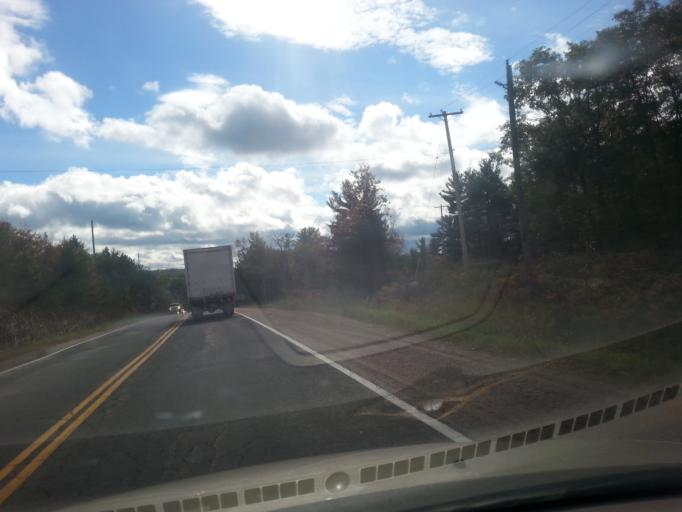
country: CA
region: Ontario
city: Pembroke
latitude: 45.6445
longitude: -77.0789
